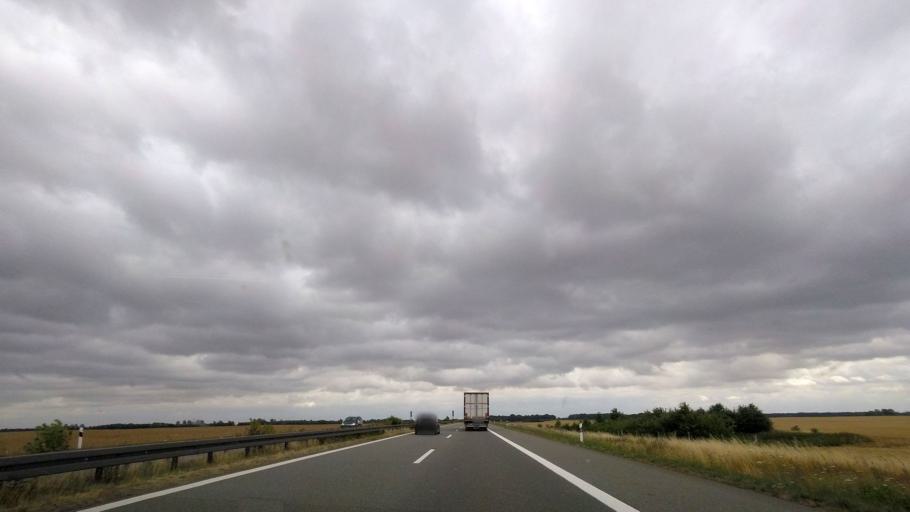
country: DE
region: Mecklenburg-Vorpommern
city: Gormin
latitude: 53.9929
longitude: 13.3310
